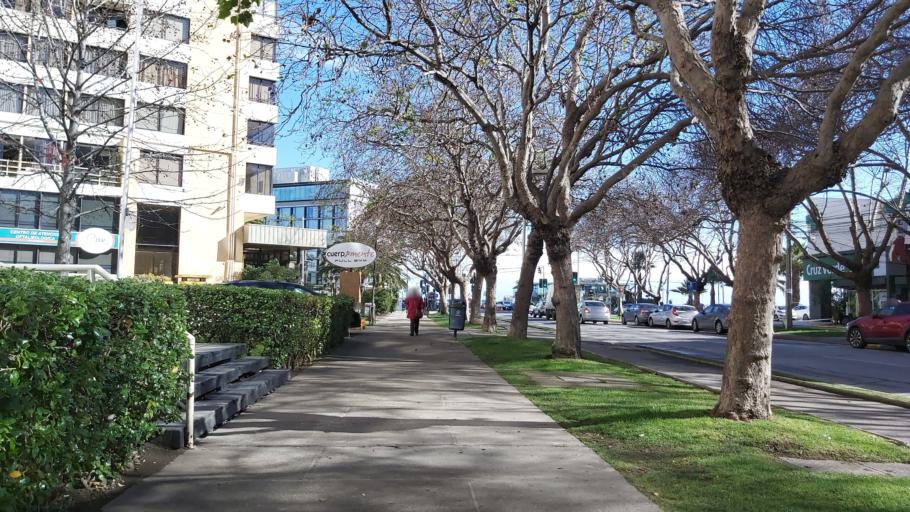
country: CL
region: Valparaiso
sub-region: Provincia de Valparaiso
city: Vina del Mar
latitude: -33.0148
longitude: -71.5541
